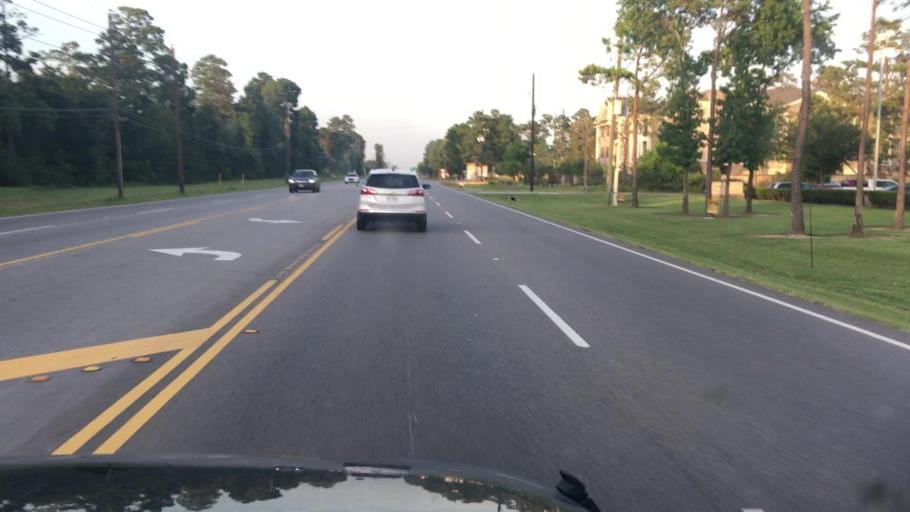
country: US
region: Texas
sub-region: Harris County
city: Atascocita
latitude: 29.9888
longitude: -95.1915
